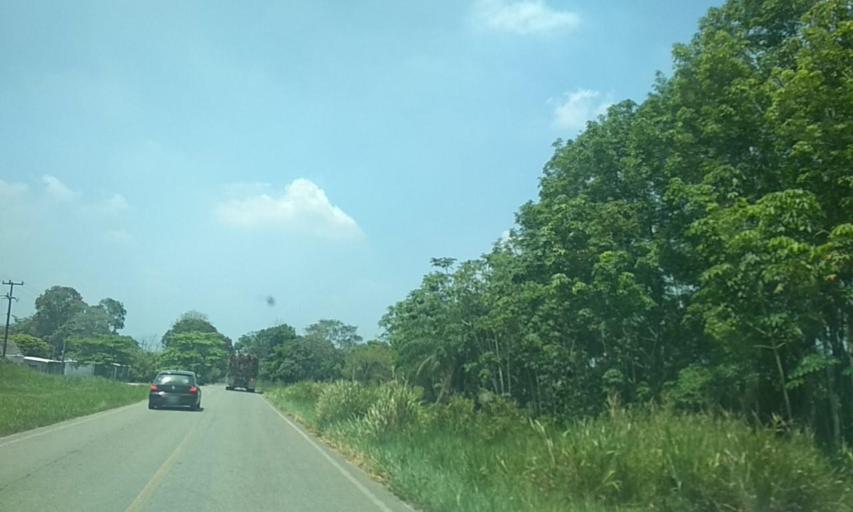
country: MX
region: Tabasco
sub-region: Huimanguillo
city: Paso de la Mina 3ra. Seccion
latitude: 17.8177
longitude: -93.6158
